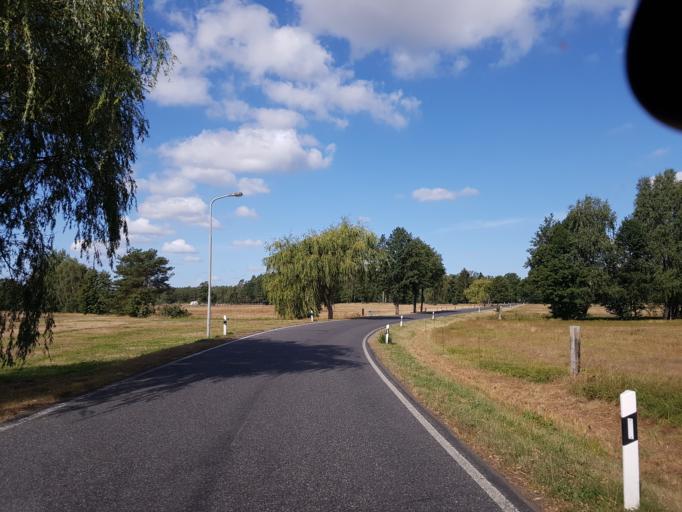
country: DE
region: Brandenburg
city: Sonnewalde
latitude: 51.7357
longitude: 13.6273
